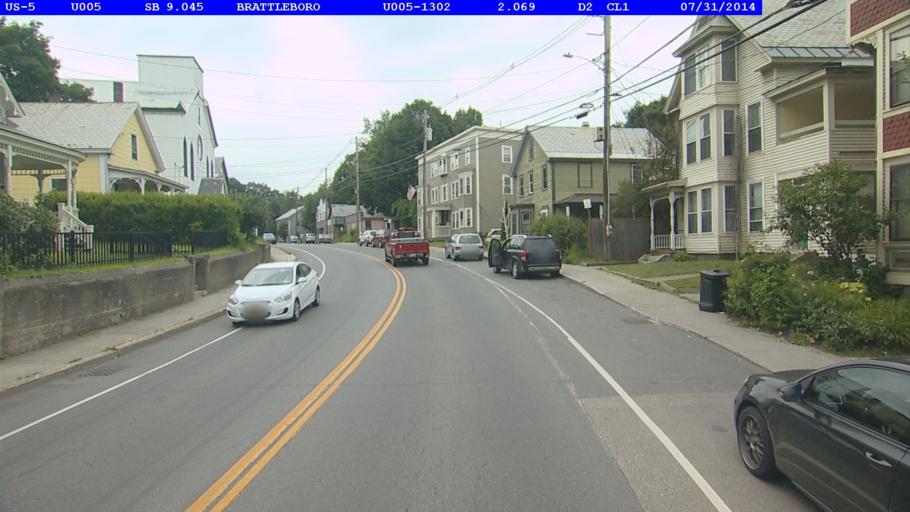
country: US
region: Vermont
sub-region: Windham County
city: Brattleboro
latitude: 42.8501
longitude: -72.5584
